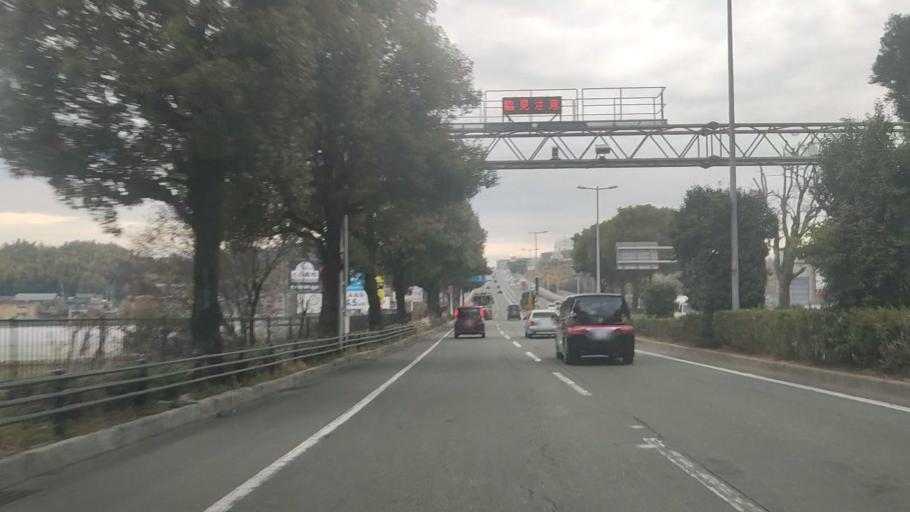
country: JP
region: Kumamoto
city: Ozu
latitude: 32.8454
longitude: 130.7814
